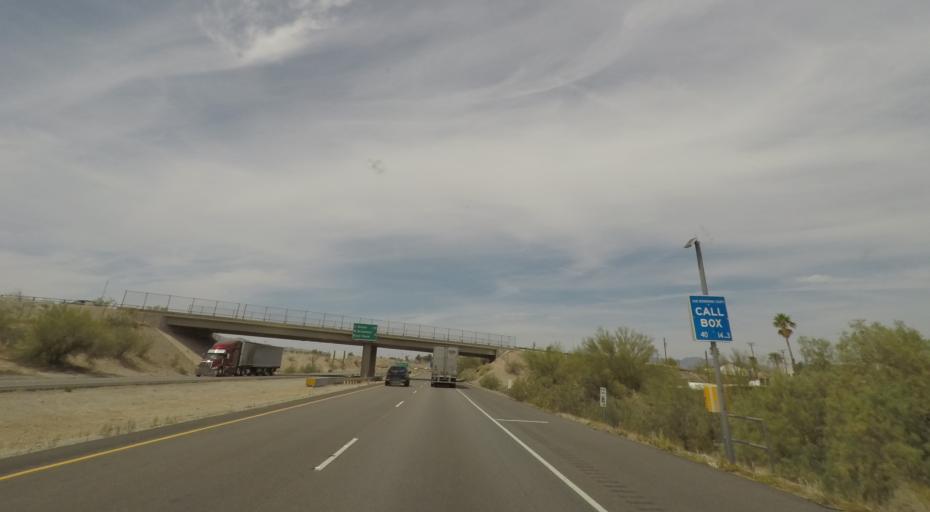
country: US
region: California
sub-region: San Bernardino County
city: Needles
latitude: 34.8327
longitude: -114.6042
